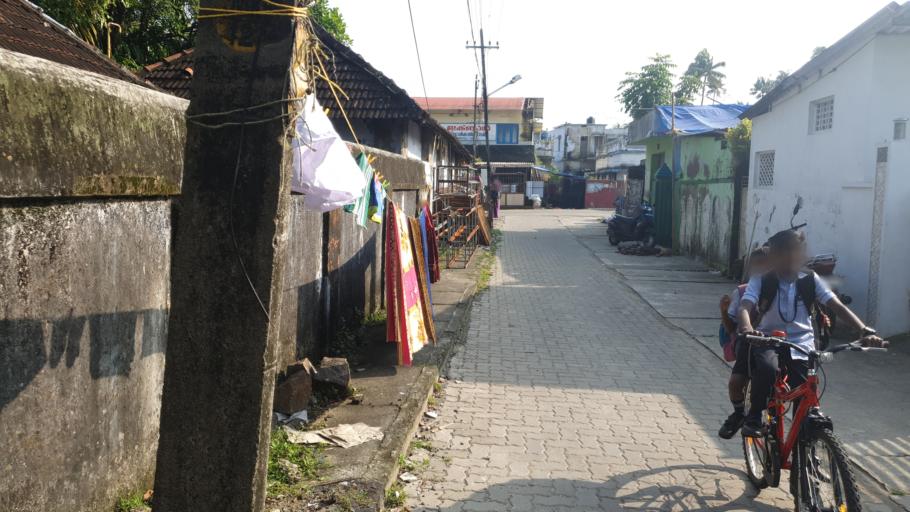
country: IN
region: Kerala
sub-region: Ernakulam
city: Cochin
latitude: 9.9613
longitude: 76.2511
